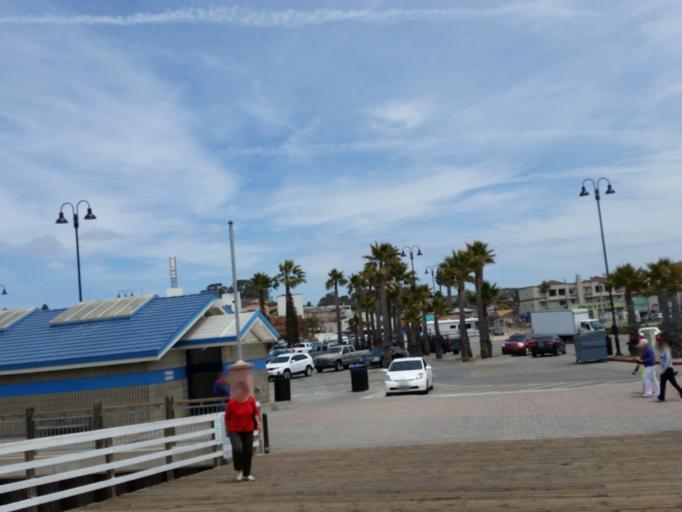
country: US
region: California
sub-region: San Luis Obispo County
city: Pismo Beach
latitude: 35.1387
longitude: -120.6432
